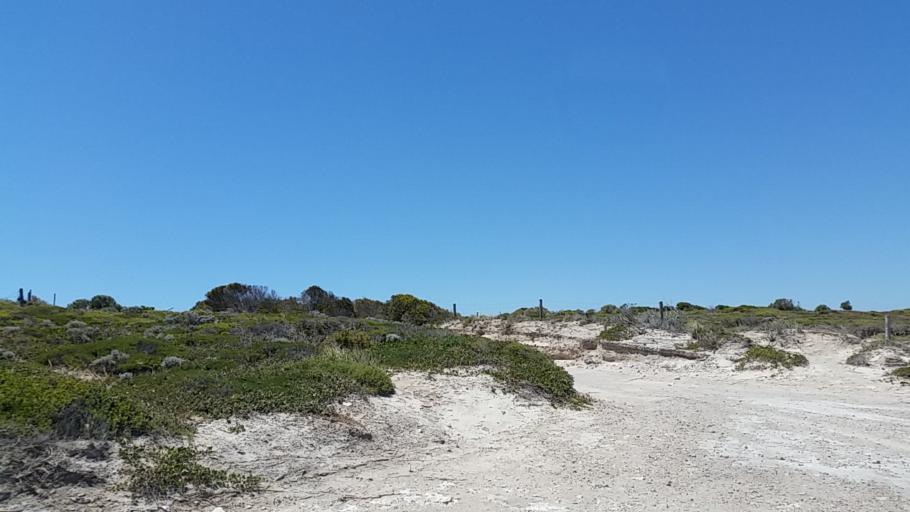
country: AU
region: South Australia
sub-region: Yorke Peninsula
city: Honiton
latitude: -35.2368
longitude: 137.1634
